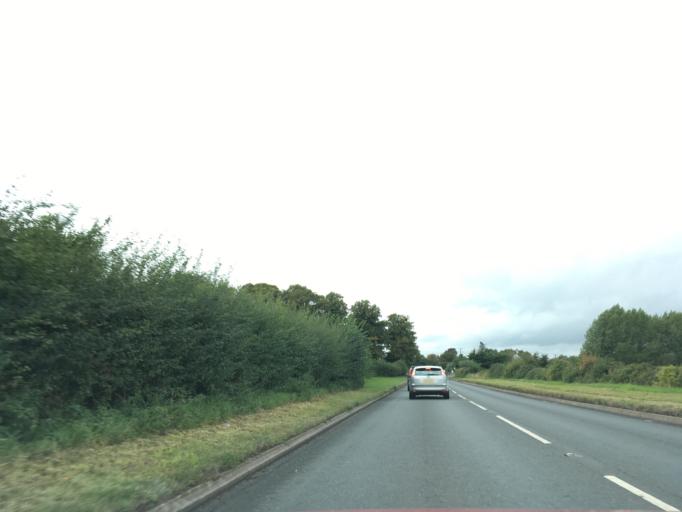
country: GB
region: England
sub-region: Herefordshire
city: Ross on Wye
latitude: 51.9124
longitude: -2.5598
